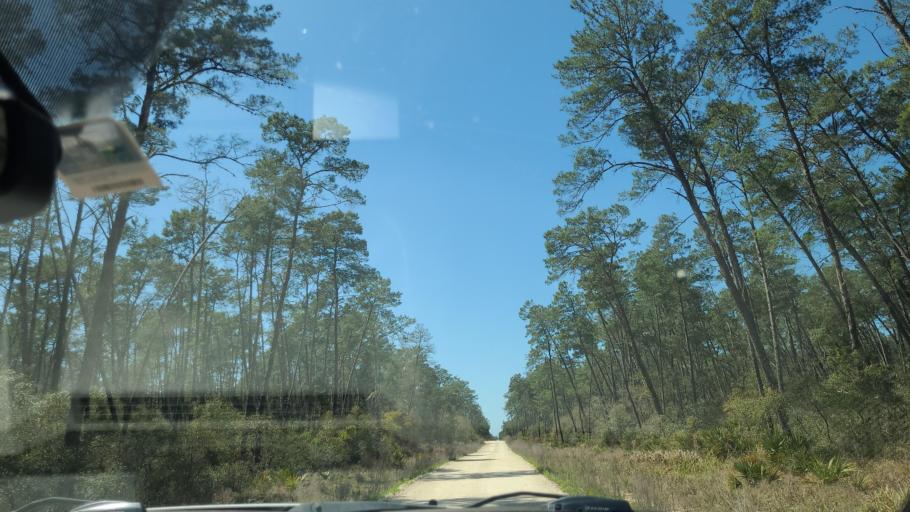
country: US
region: Florida
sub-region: Putnam County
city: Interlachen
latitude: 29.4283
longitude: -81.8824
